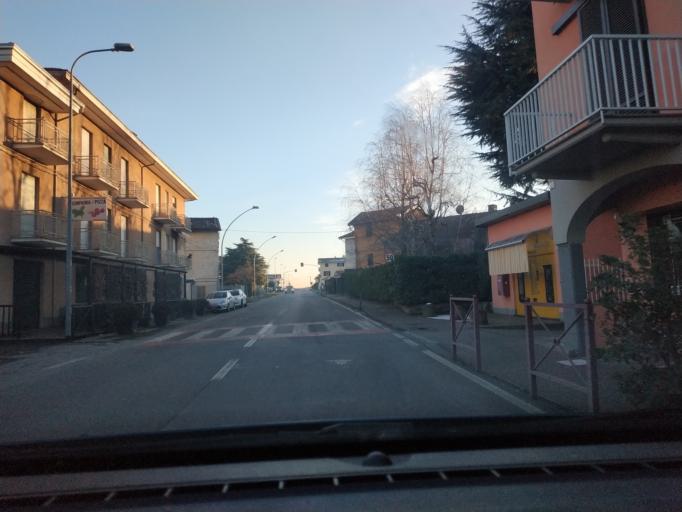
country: IT
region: Piedmont
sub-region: Provincia di Torino
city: Romano Canavese
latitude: 45.4267
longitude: 7.8825
